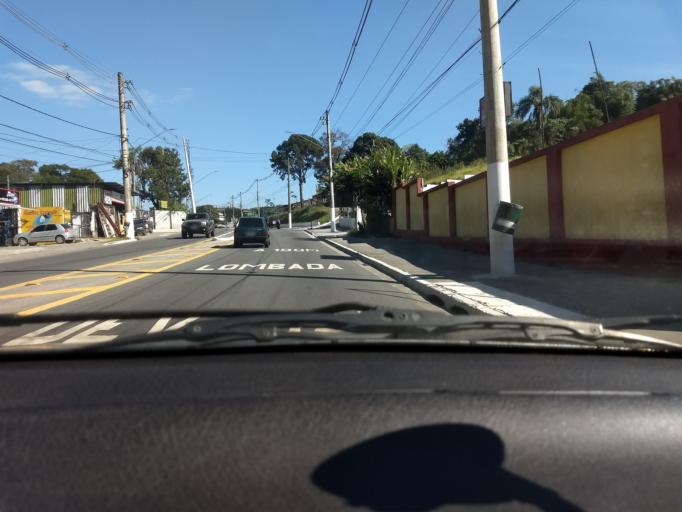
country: BR
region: Sao Paulo
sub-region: Embu-Guacu
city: Embu Guacu
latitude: -23.8056
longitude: -46.7360
